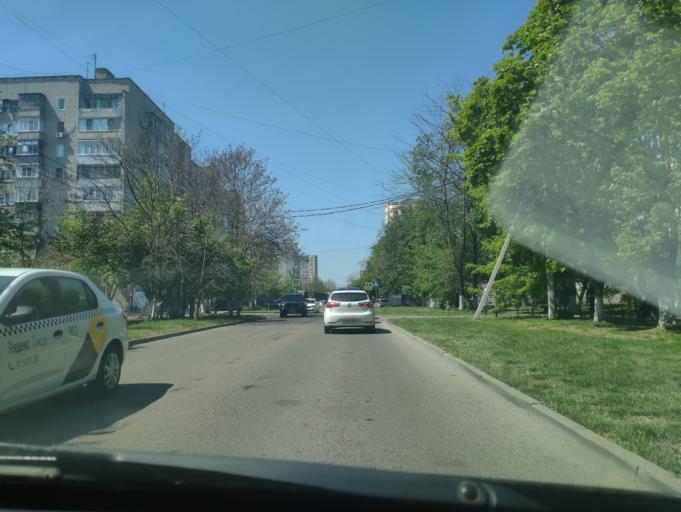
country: RU
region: Krasnodarskiy
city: Krasnodar
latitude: 45.0625
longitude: 39.0049
